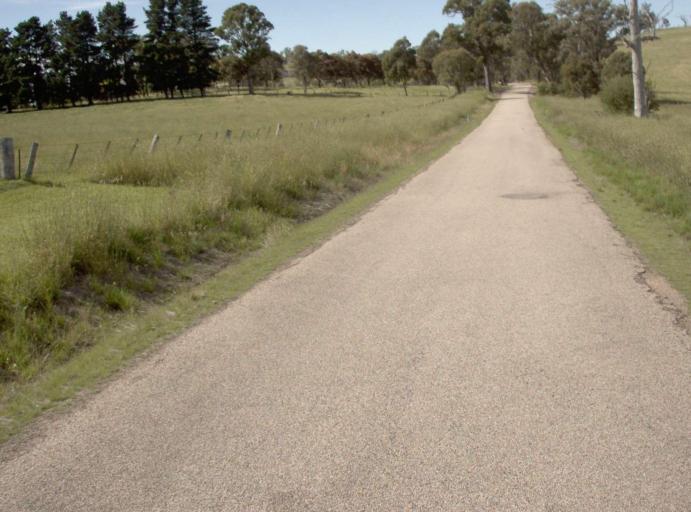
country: AU
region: Victoria
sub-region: East Gippsland
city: Lakes Entrance
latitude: -37.5021
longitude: 148.1330
